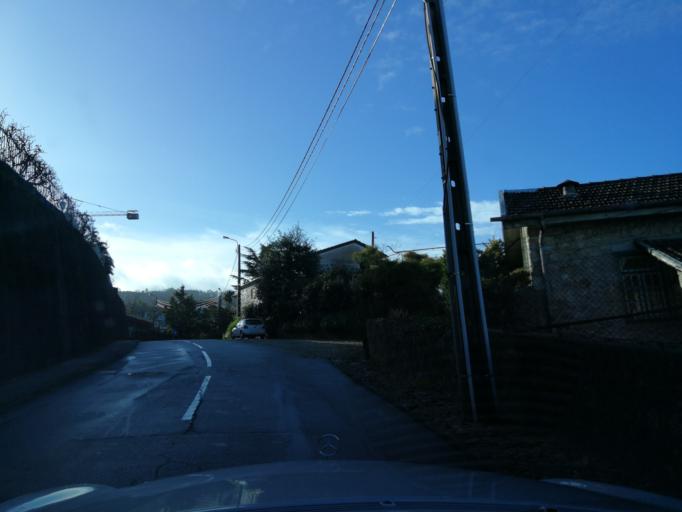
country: PT
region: Braga
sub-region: Braga
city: Braga
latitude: 41.5495
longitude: -8.3882
